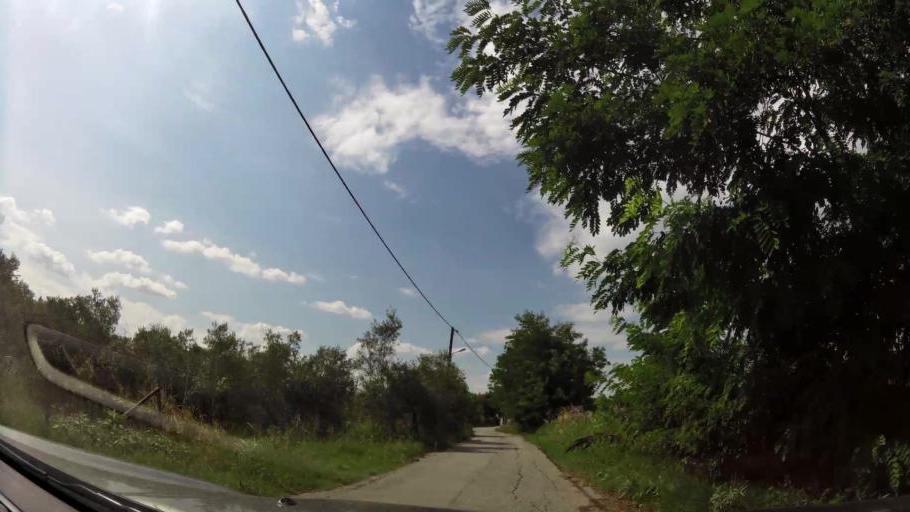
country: GR
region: Central Macedonia
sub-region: Nomos Pierias
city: Makrygialos
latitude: 40.4118
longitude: 22.6046
